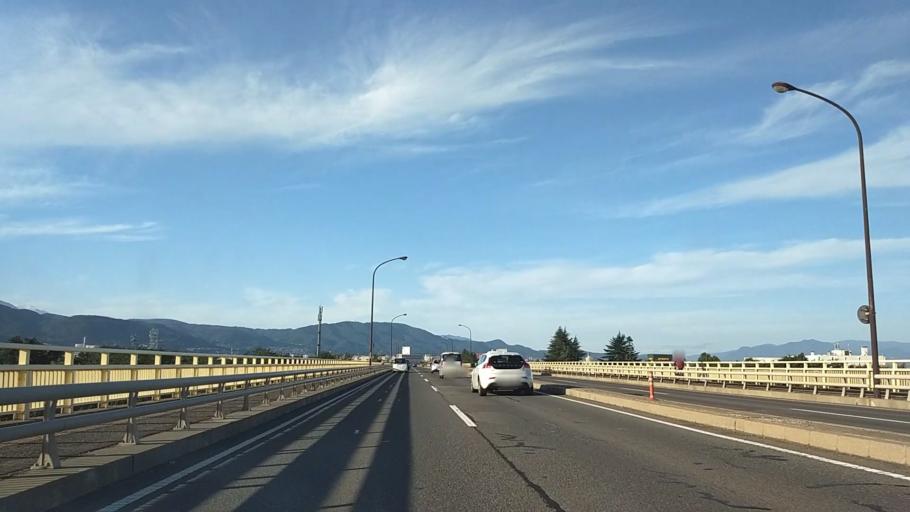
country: JP
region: Nagano
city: Nagano-shi
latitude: 36.6192
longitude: 138.1987
